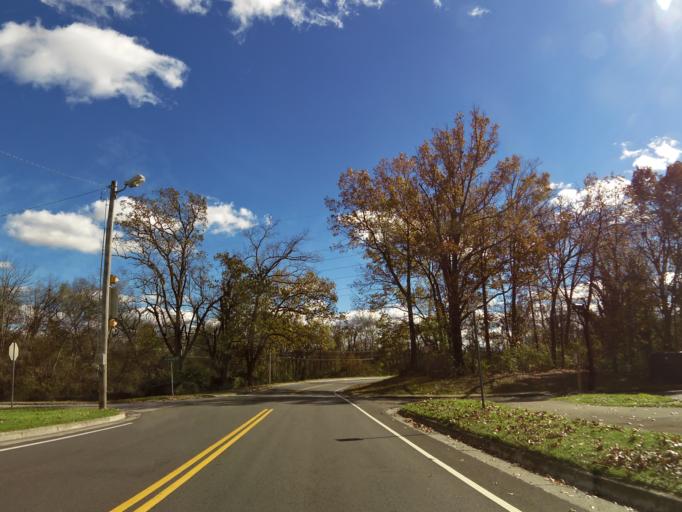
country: US
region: Tennessee
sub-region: Blount County
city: Alcoa
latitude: 35.7937
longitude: -83.9719
